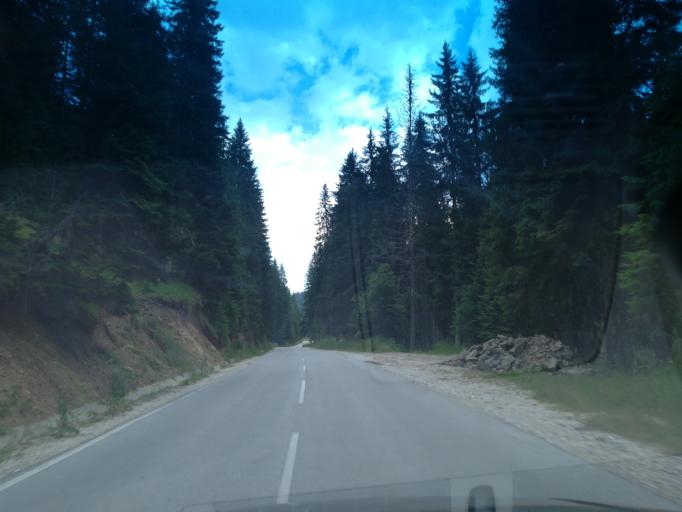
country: BG
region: Smolyan
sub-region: Obshtina Chepelare
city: Chepelare
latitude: 41.6608
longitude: 24.6809
